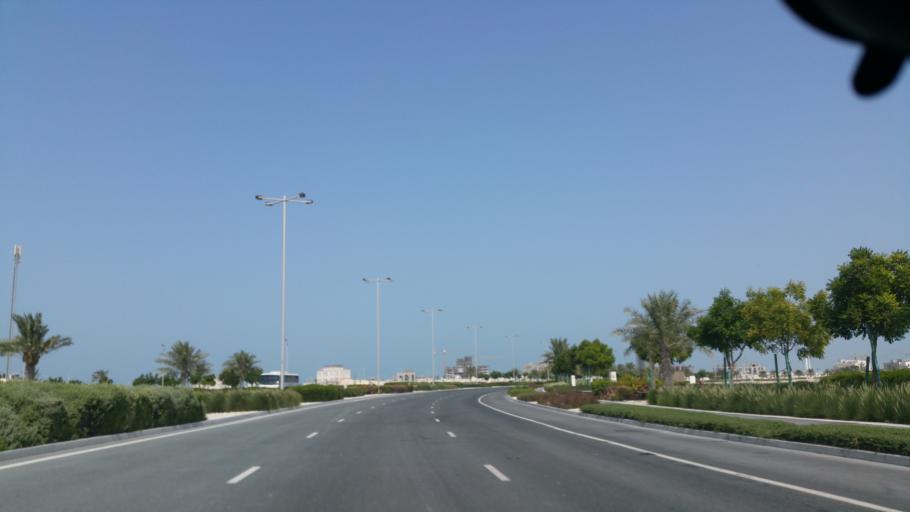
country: QA
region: Baladiyat Umm Salal
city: Umm Salal Muhammad
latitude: 25.4410
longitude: 51.5093
